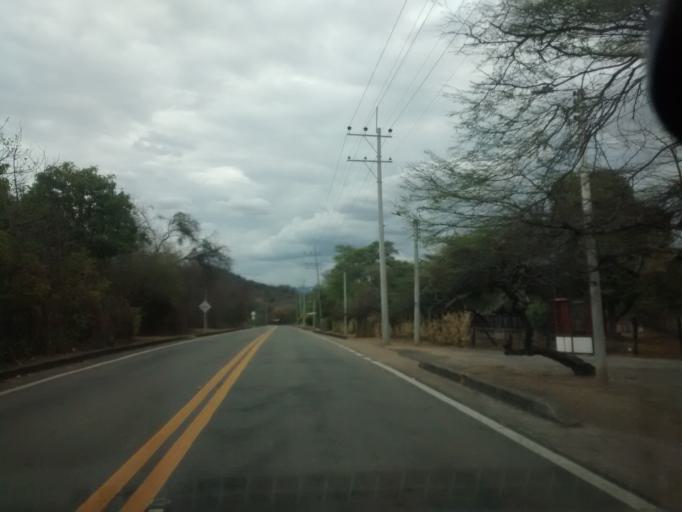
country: CO
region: Cundinamarca
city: Agua de Dios
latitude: 4.4287
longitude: -74.6914
